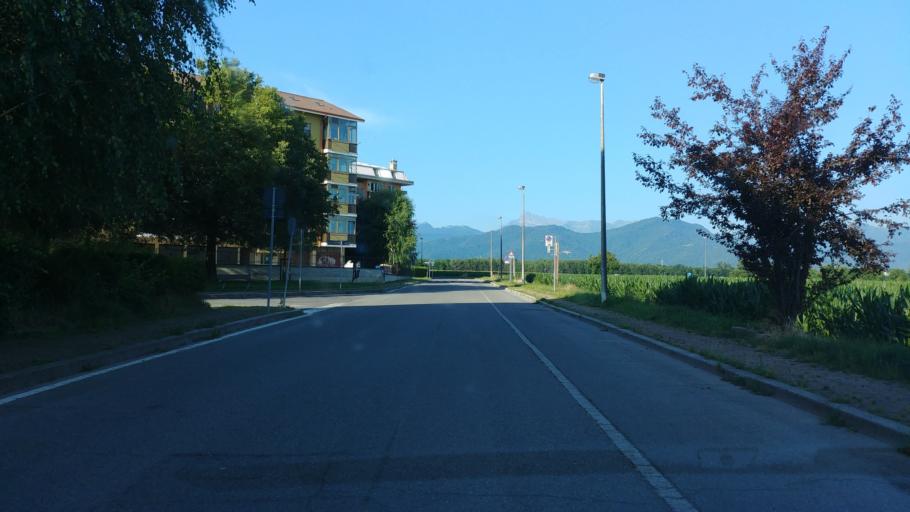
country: IT
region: Piedmont
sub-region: Provincia di Cuneo
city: San Defendente
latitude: 44.3973
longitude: 7.5183
